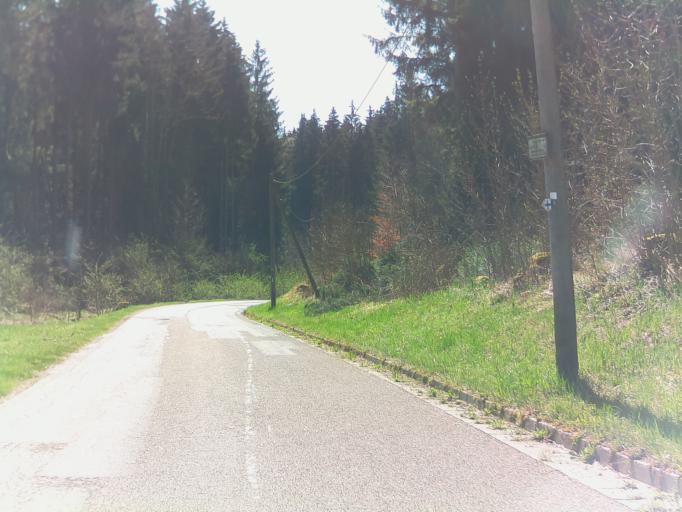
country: DE
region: Bavaria
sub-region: Upper Palatinate
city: Kastl
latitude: 49.3932
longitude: 11.6803
